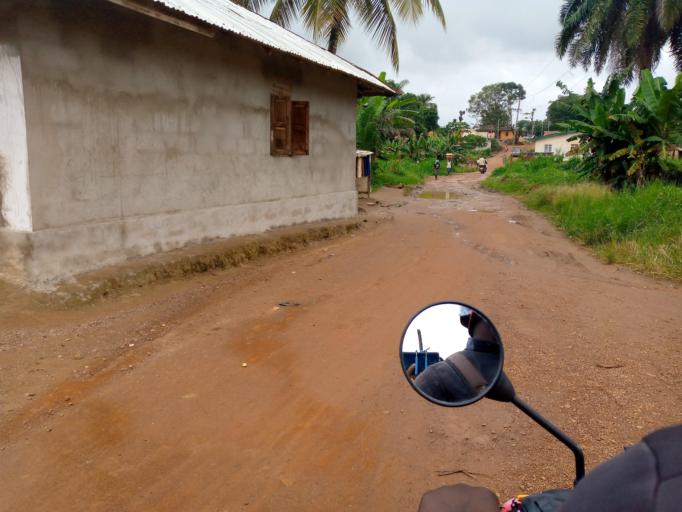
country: SL
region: Eastern Province
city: Kenema
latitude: 7.8641
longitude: -11.1923
